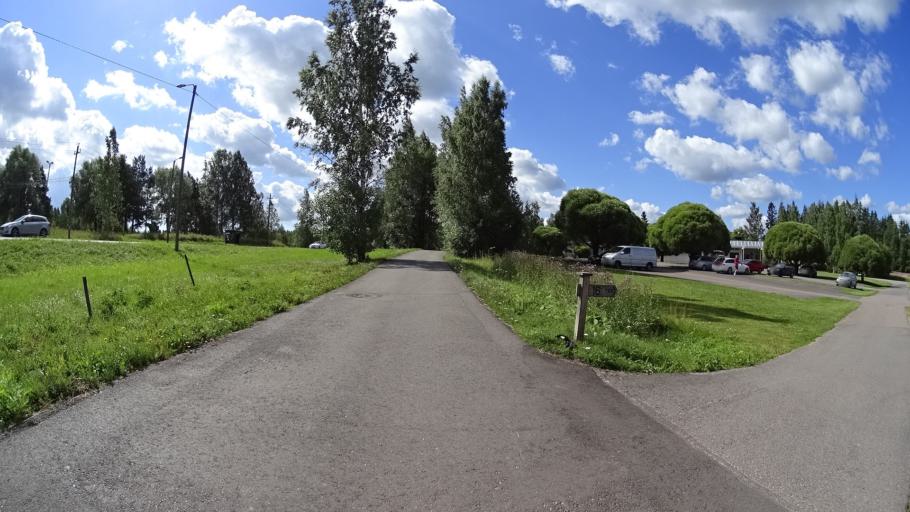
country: FI
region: Uusimaa
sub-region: Helsinki
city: Tuusula
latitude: 60.4160
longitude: 25.0514
